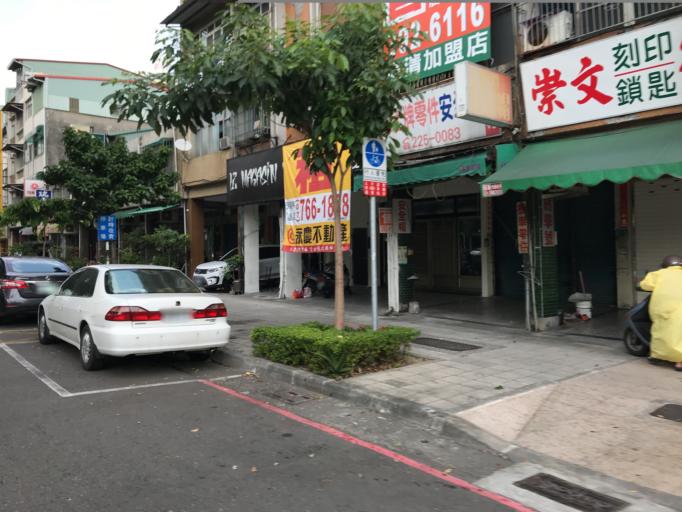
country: TW
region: Kaohsiung
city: Kaohsiung
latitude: 22.6344
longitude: 120.3137
